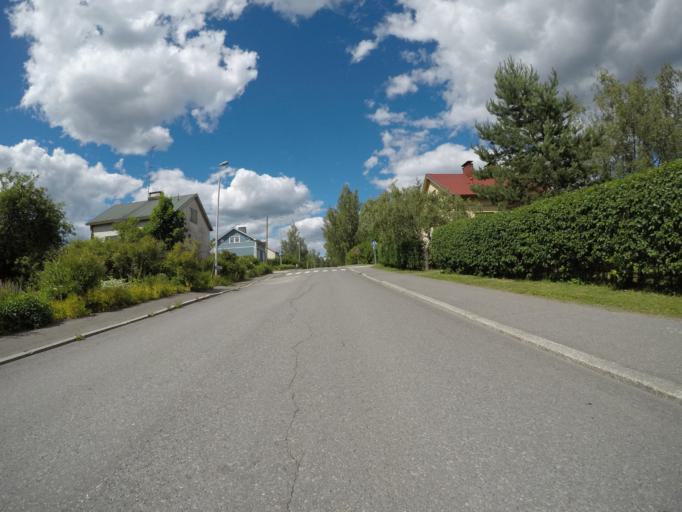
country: FI
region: Haeme
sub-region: Haemeenlinna
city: Haemeenlinna
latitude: 61.0006
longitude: 24.4467
